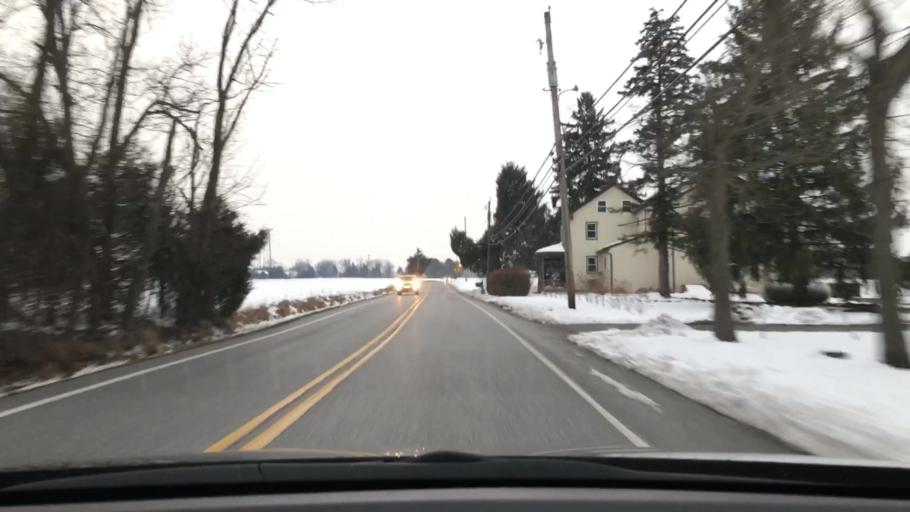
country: US
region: Pennsylvania
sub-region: York County
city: Dover
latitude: 39.9826
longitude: -76.8507
